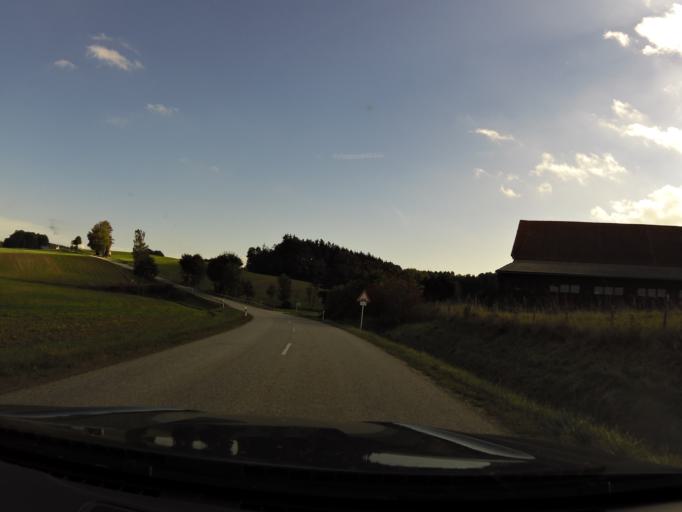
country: DE
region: Bavaria
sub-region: Lower Bavaria
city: Tiefenbach
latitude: 48.4813
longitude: 12.1150
